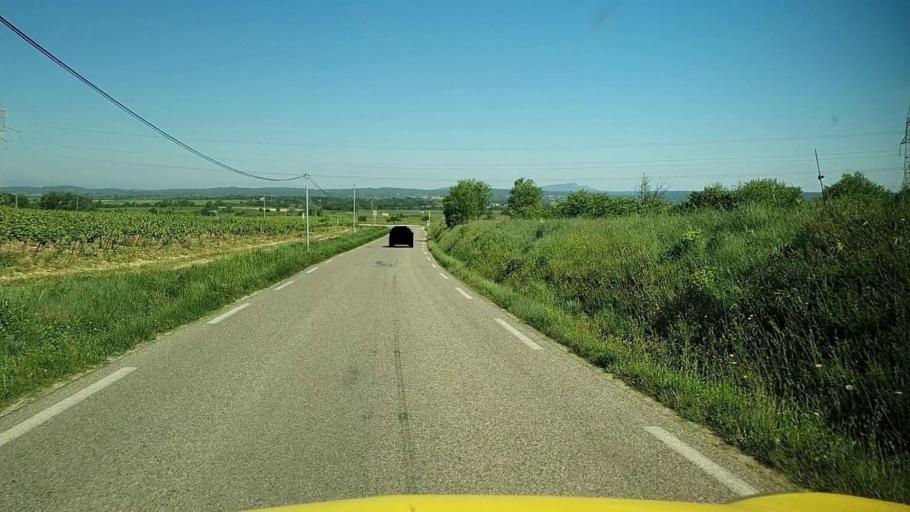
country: FR
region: Languedoc-Roussillon
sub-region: Departement du Gard
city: Blauzac
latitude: 43.9468
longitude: 4.3462
